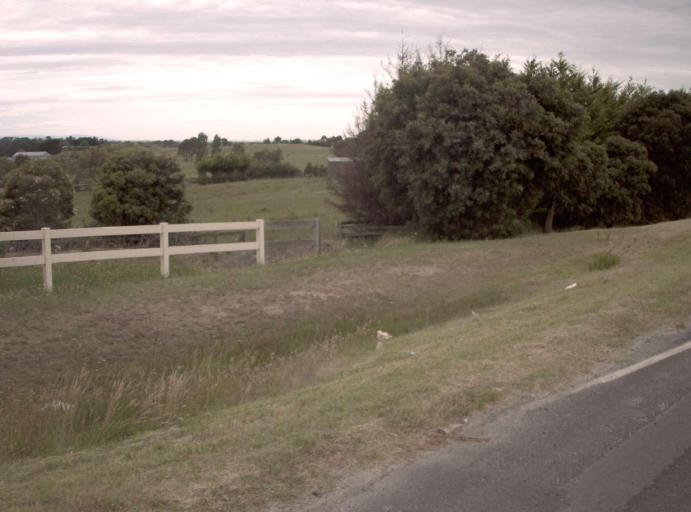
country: AU
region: Victoria
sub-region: Casey
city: Junction Village
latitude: -38.1410
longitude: 145.3074
